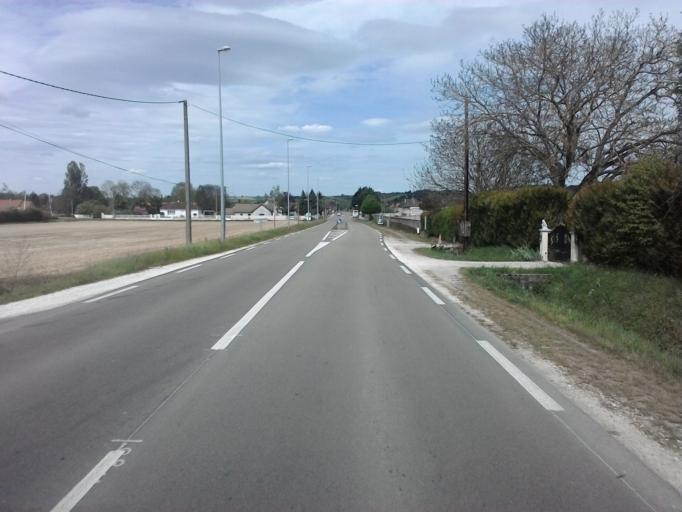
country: FR
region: Bourgogne
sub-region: Departement de l'Yonne
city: Augy
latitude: 47.7617
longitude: 3.6104
